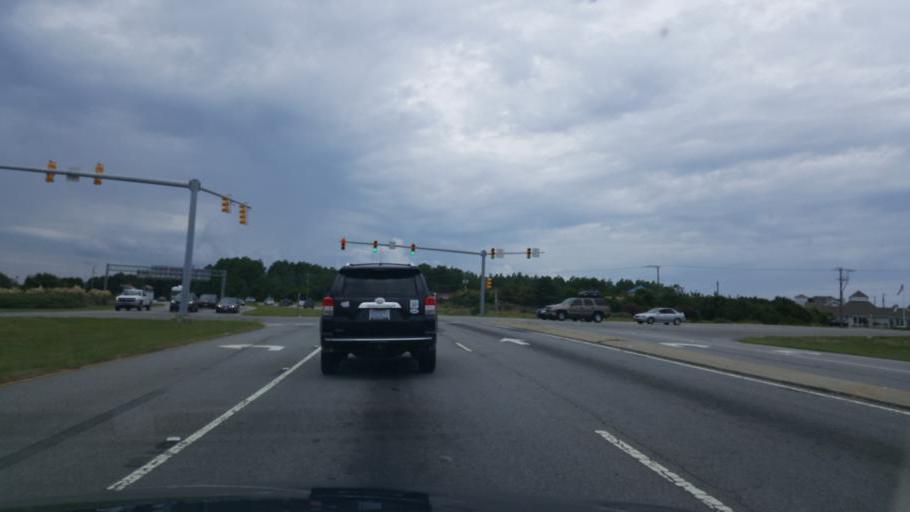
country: US
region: North Carolina
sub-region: Dare County
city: Kitty Hawk
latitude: 36.0991
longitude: -75.7142
